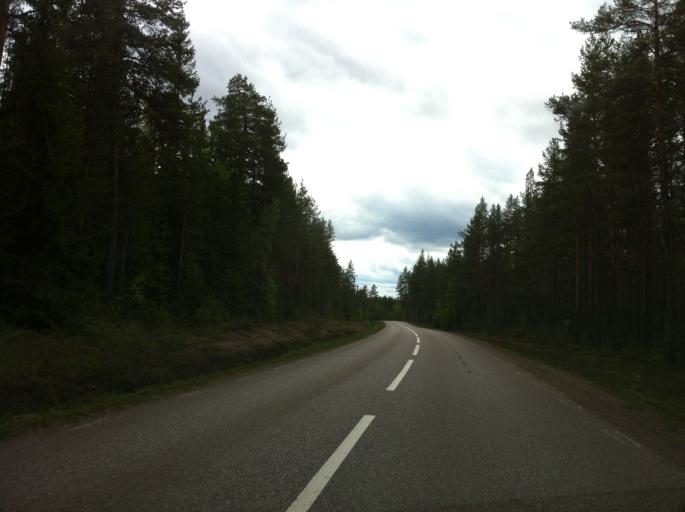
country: NO
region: Hedmark
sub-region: Trysil
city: Innbygda
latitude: 61.4806
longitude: 13.0836
